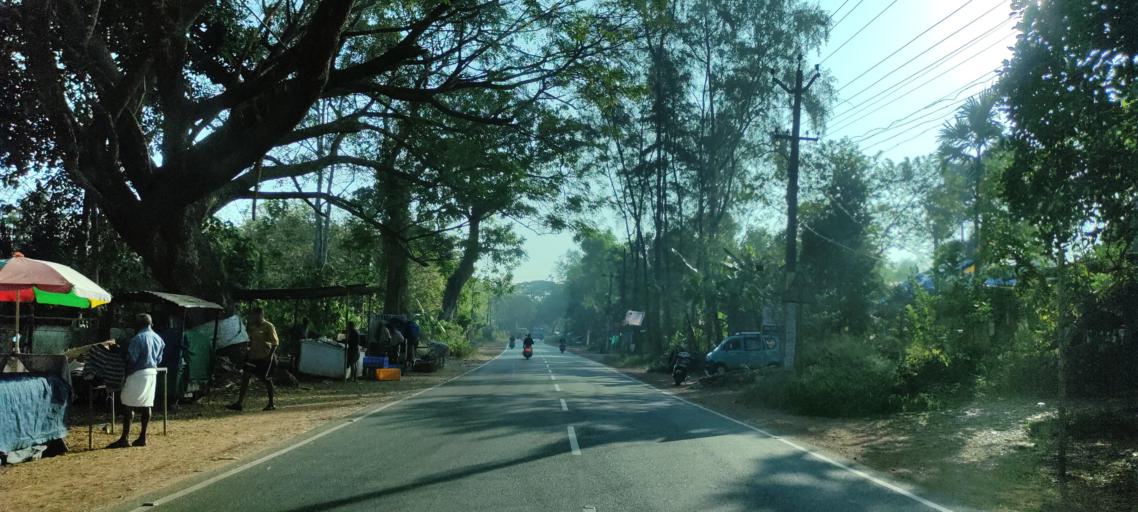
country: IN
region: Kerala
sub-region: Alappuzha
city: Kattanam
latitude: 9.1750
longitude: 76.6197
